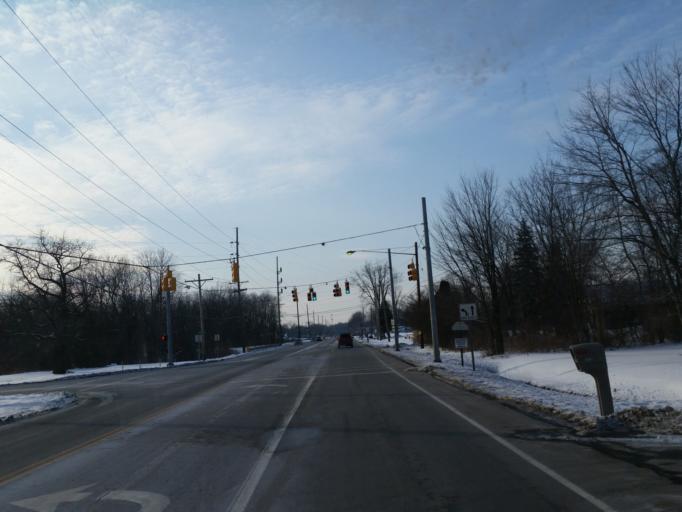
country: US
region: Ohio
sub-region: Lorain County
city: Sheffield Lake
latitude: 41.4608
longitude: -82.1074
